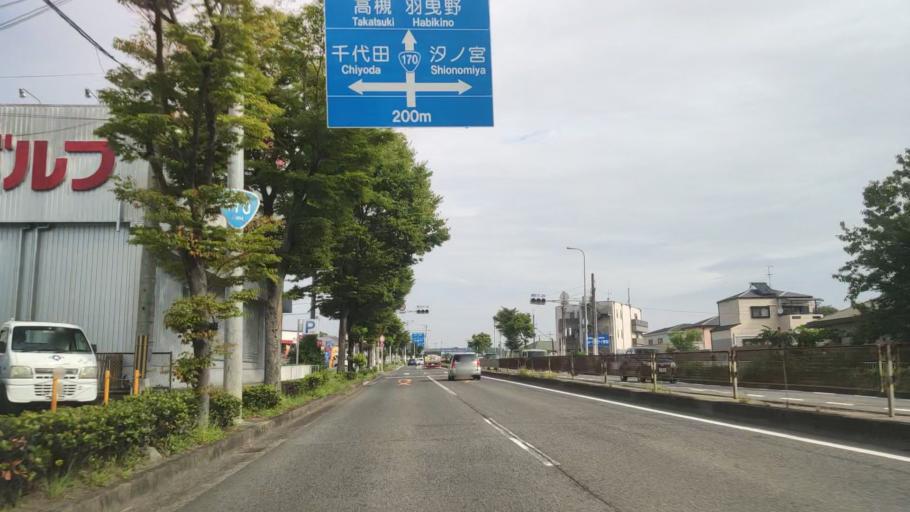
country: JP
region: Osaka
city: Tondabayashicho
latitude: 34.4658
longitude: 135.5751
